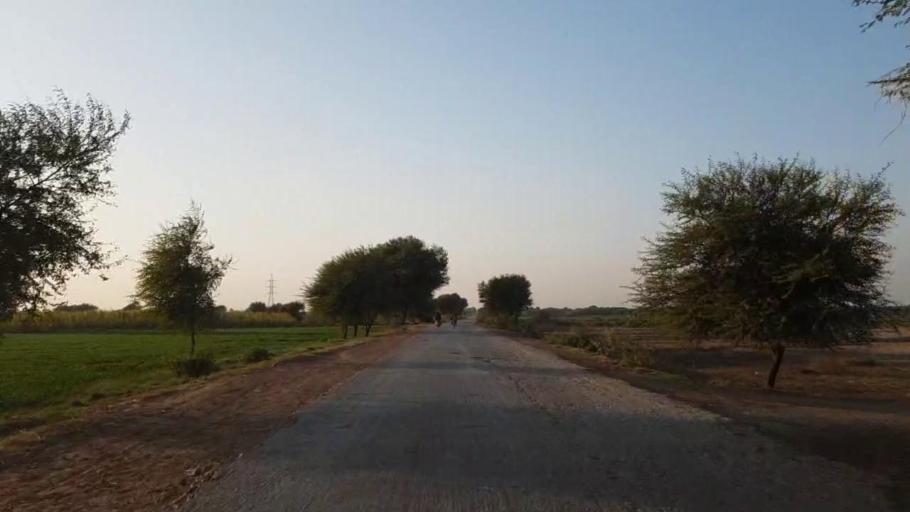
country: PK
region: Sindh
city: Chambar
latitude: 25.2290
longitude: 68.7088
